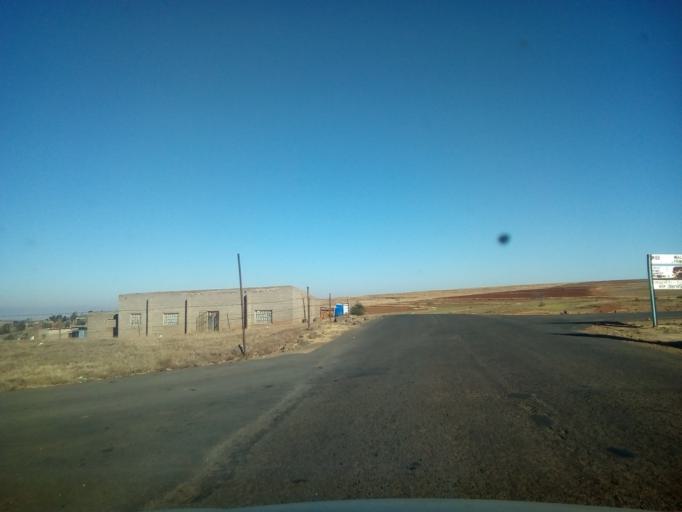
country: LS
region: Berea
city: Teyateyaneng
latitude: -29.2826
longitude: 27.6604
